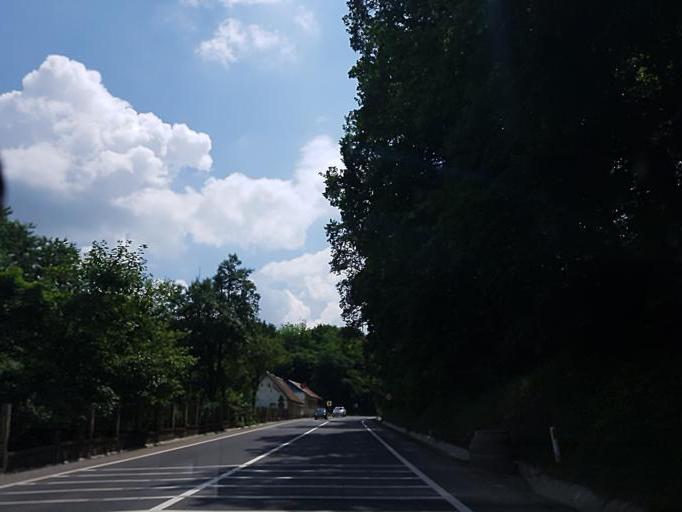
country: RO
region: Sibiu
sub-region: Comuna Slimnic
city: Slimnic
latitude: 45.9391
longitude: 24.1720
